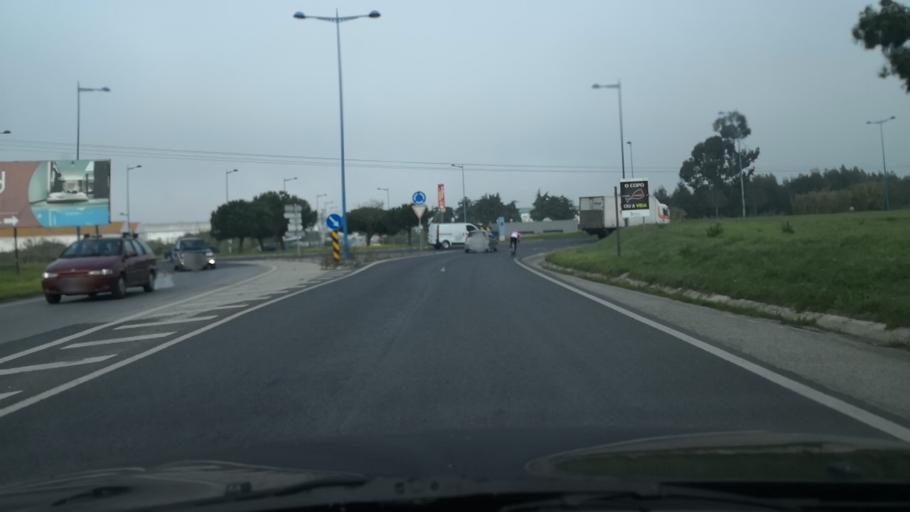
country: PT
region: Setubal
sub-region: Montijo
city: Montijo
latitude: 38.6928
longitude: -8.9502
